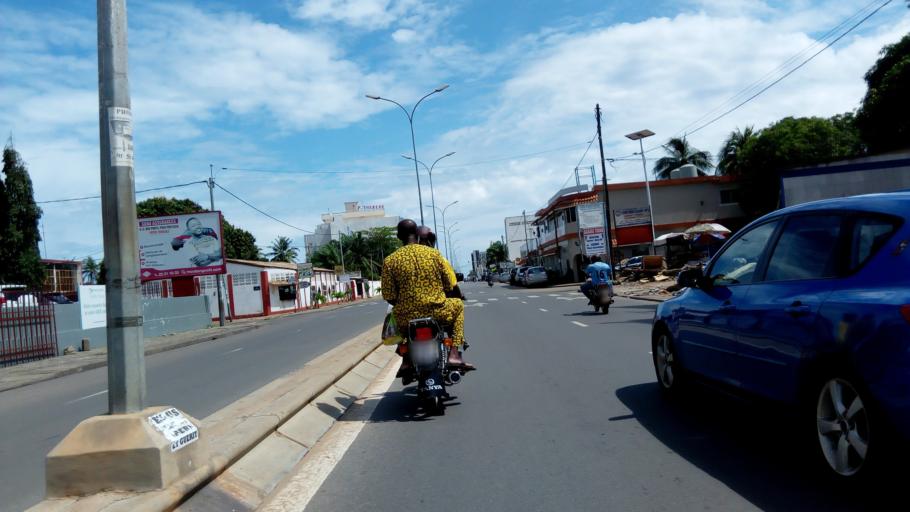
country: TG
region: Maritime
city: Lome
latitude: 6.1252
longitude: 1.2094
